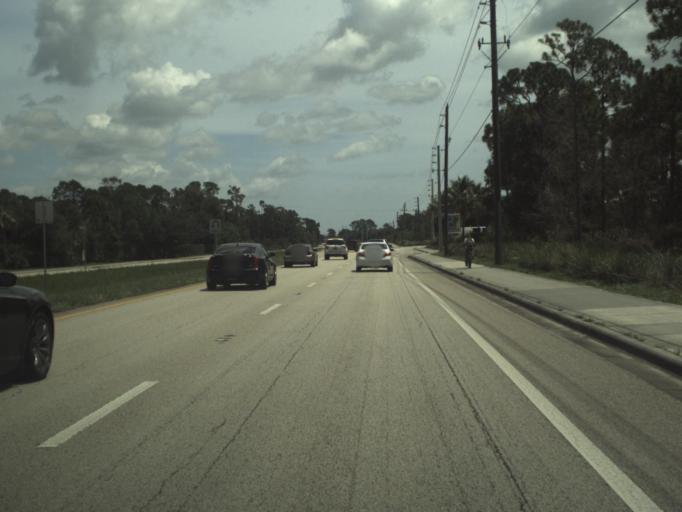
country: US
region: Florida
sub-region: Martin County
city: Palm City
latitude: 27.1402
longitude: -80.2475
